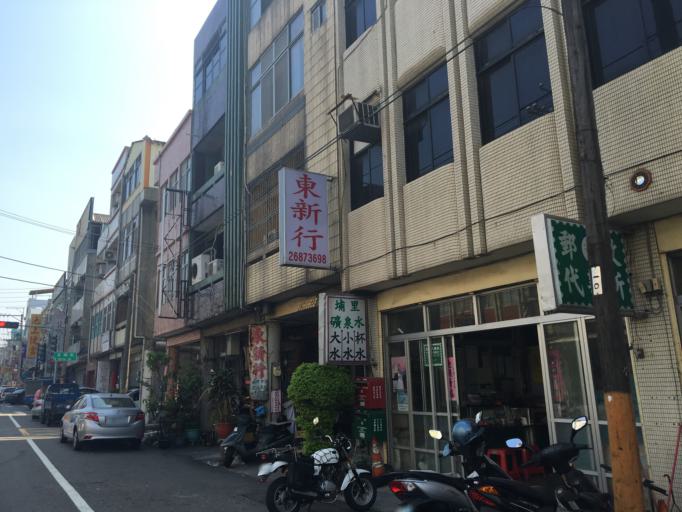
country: TW
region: Taiwan
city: Fengyuan
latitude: 24.3458
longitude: 120.6188
